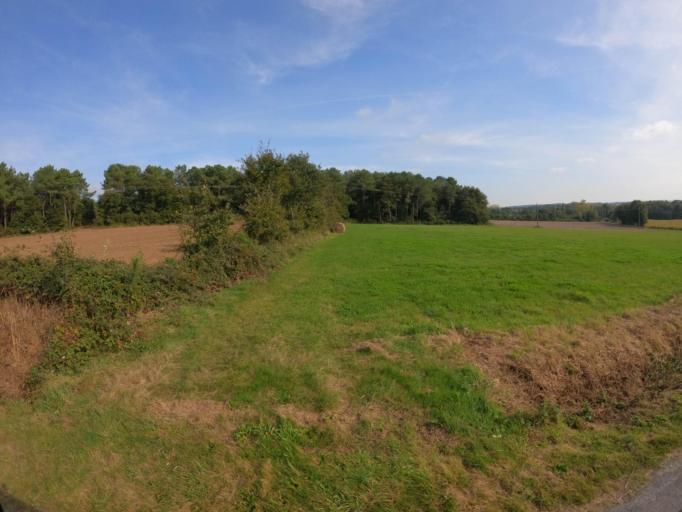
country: FR
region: Brittany
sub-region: Departement du Morbihan
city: Ploermel
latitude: 47.8765
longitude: -2.4040
